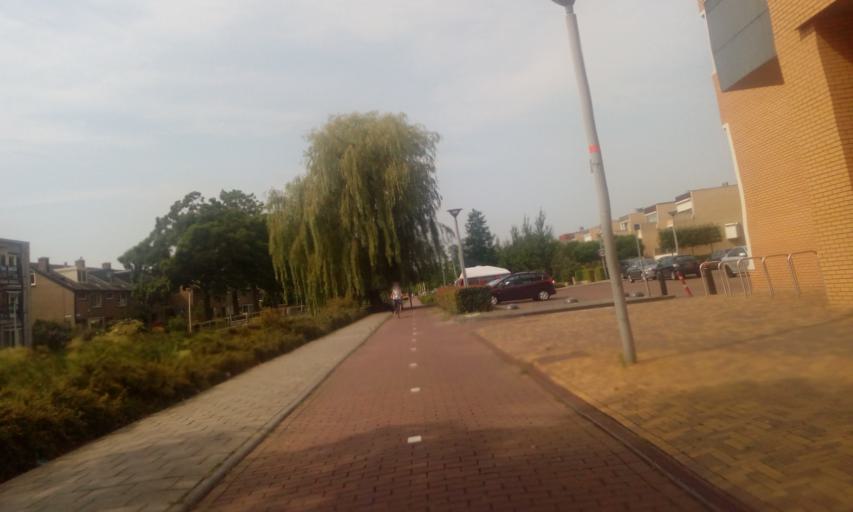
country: NL
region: South Holland
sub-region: Gemeente Capelle aan den IJssel
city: Capelle aan den IJssel
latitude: 51.9655
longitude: 4.6071
